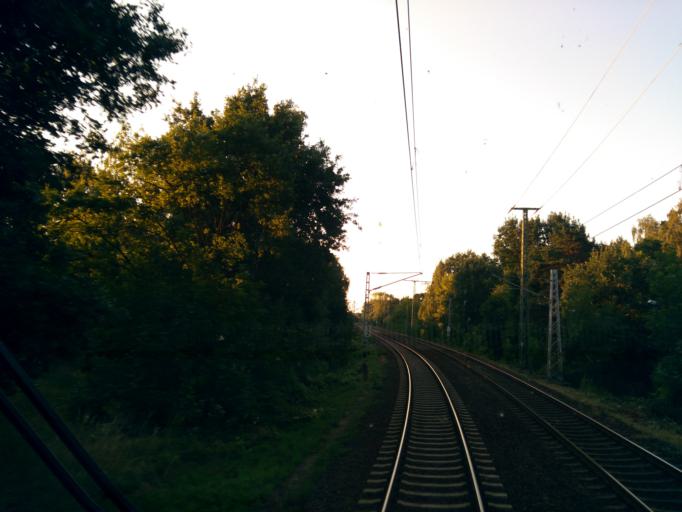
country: DE
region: Berlin
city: Adlershof
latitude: 52.4183
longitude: 13.5596
